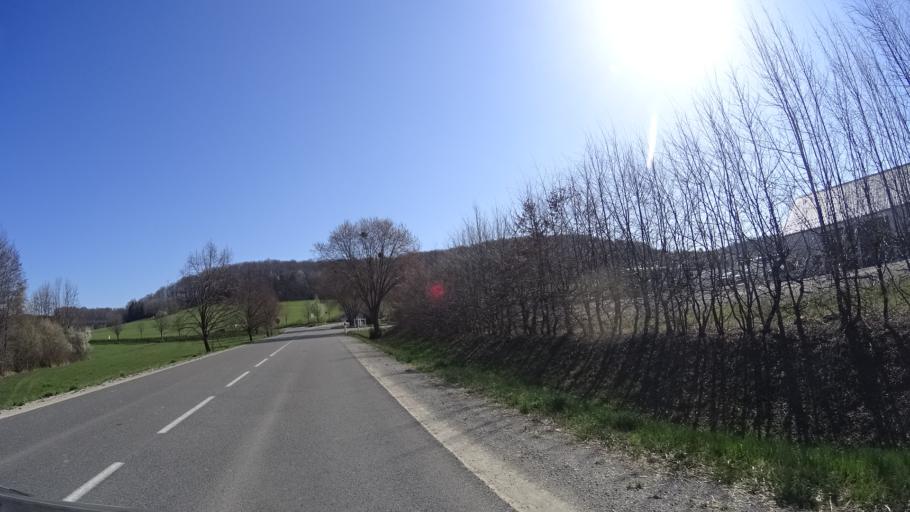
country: FR
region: Franche-Comte
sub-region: Departement du Doubs
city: Mamirolle
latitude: 47.1607
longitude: 6.1101
